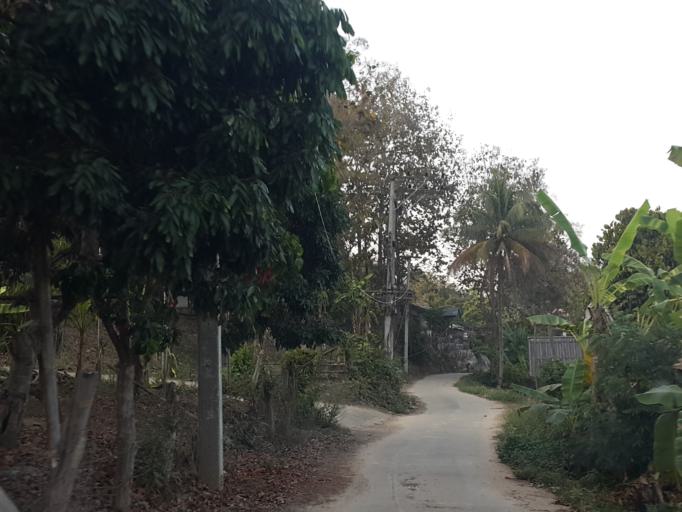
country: TH
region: Chiang Mai
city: Mae Taeng
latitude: 19.1104
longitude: 98.8284
